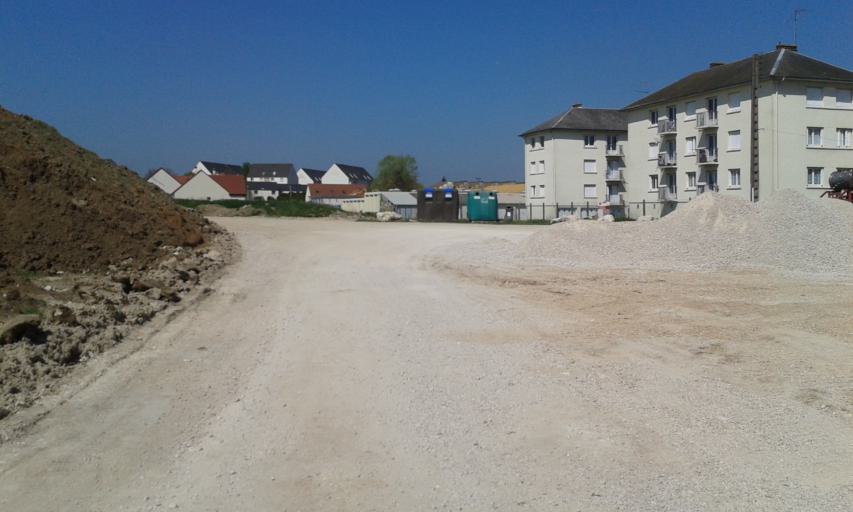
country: FR
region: Centre
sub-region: Departement du Loiret
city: Beaugency
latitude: 47.7792
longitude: 1.6210
